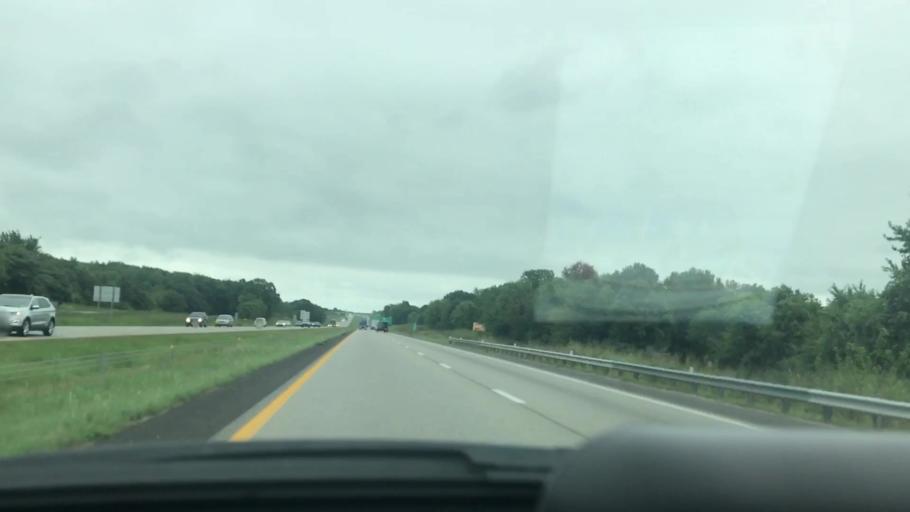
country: US
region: Missouri
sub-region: Greene County
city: Republic
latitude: 37.1919
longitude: -93.4637
